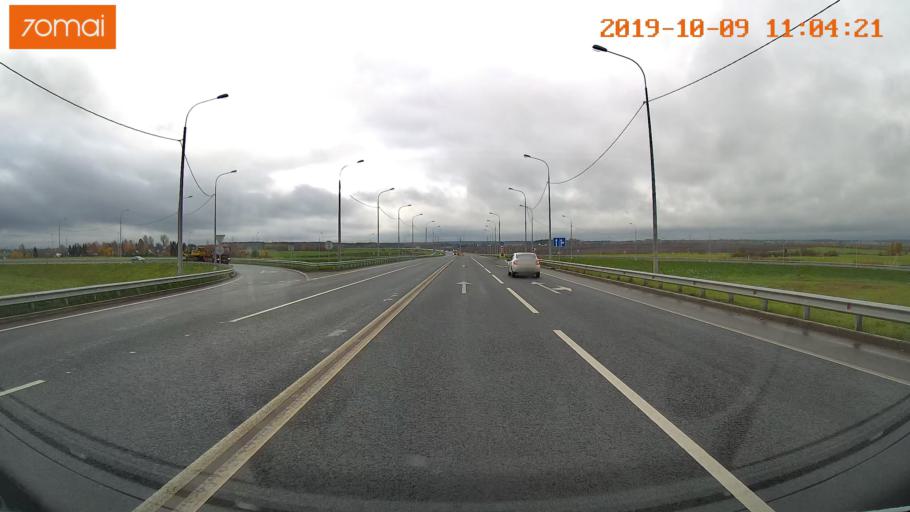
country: RU
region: Vologda
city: Vologda
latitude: 59.2128
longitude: 39.7682
